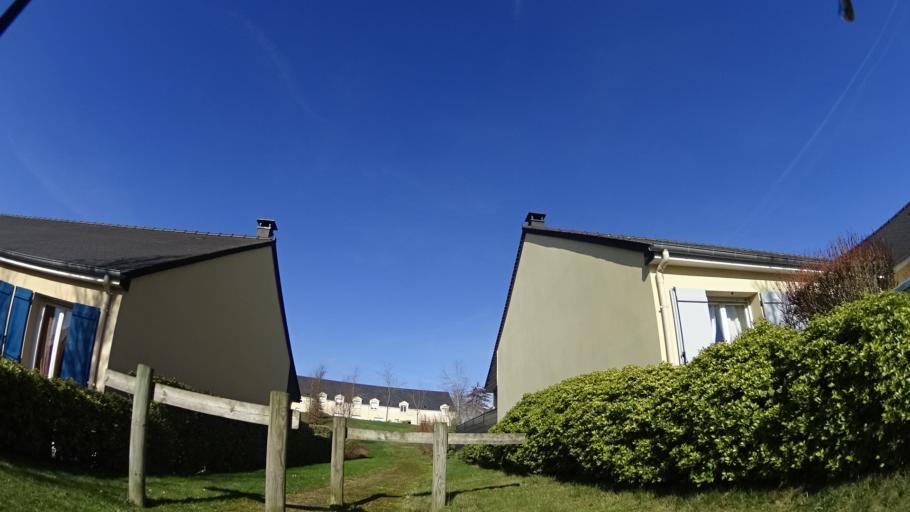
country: FR
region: Brittany
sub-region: Departement d'Ille-et-Vilaine
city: Geveze
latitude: 48.2230
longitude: -1.7983
